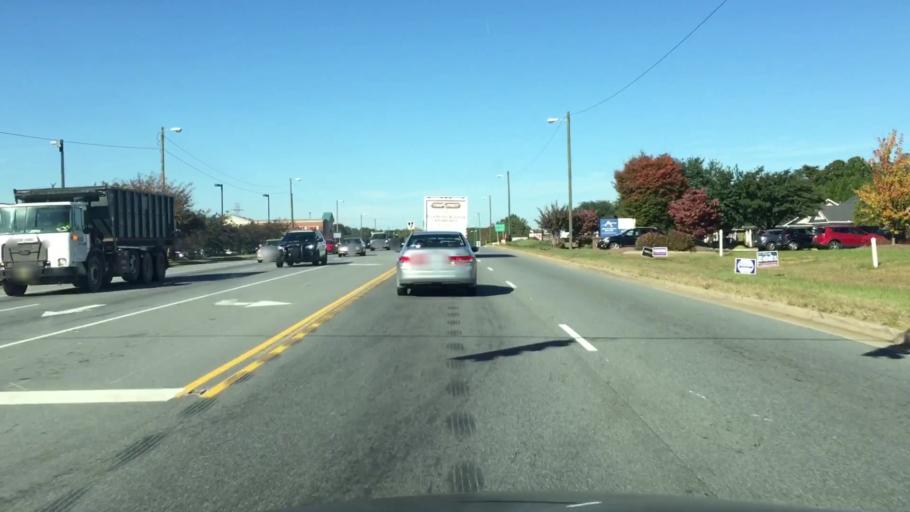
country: US
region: North Carolina
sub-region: Rowan County
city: Salisbury
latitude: 35.6581
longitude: -80.5003
